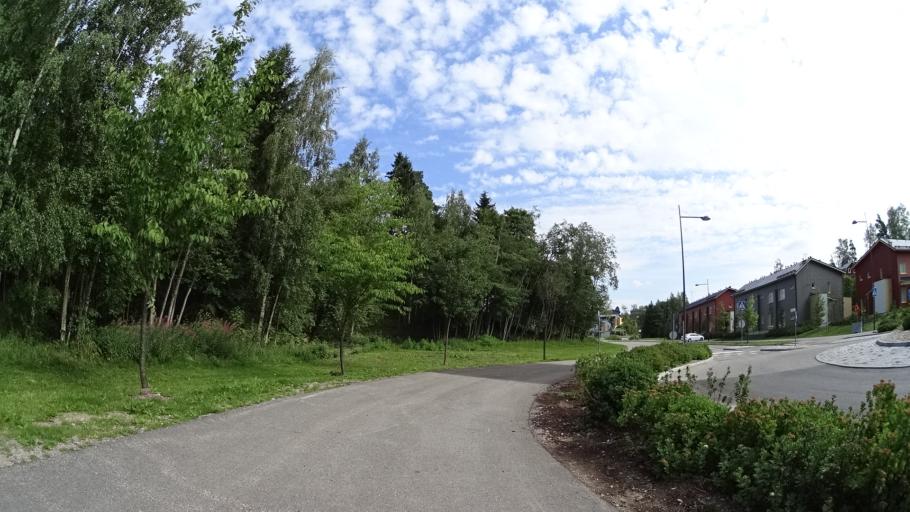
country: FI
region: Uusimaa
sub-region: Helsinki
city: Espoo
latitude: 60.1921
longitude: 24.5917
